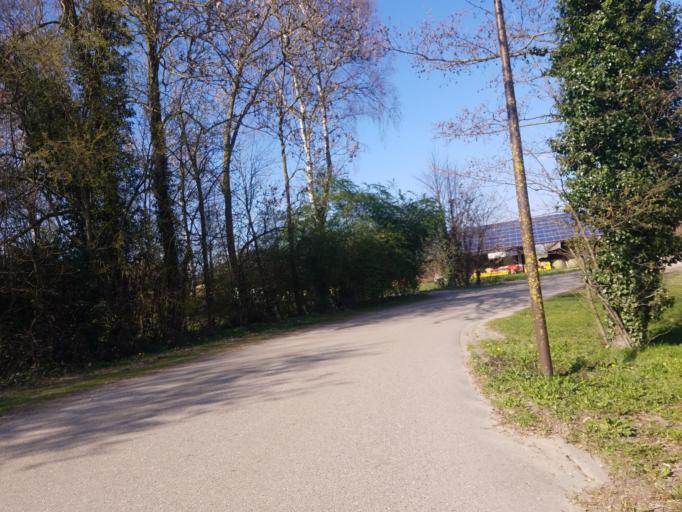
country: DE
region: Baden-Wuerttemberg
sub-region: Karlsruhe Region
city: Schwarzach
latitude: 48.7480
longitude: 8.0606
